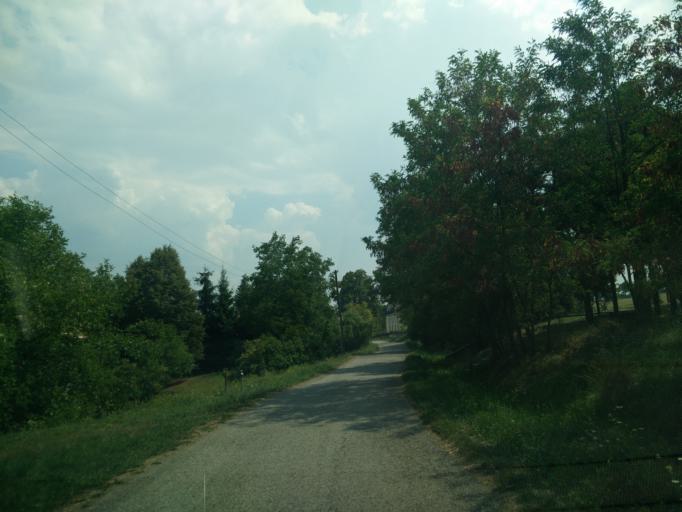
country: SK
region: Banskobystricky
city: Ziar nad Hronom
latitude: 48.5790
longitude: 18.7561
